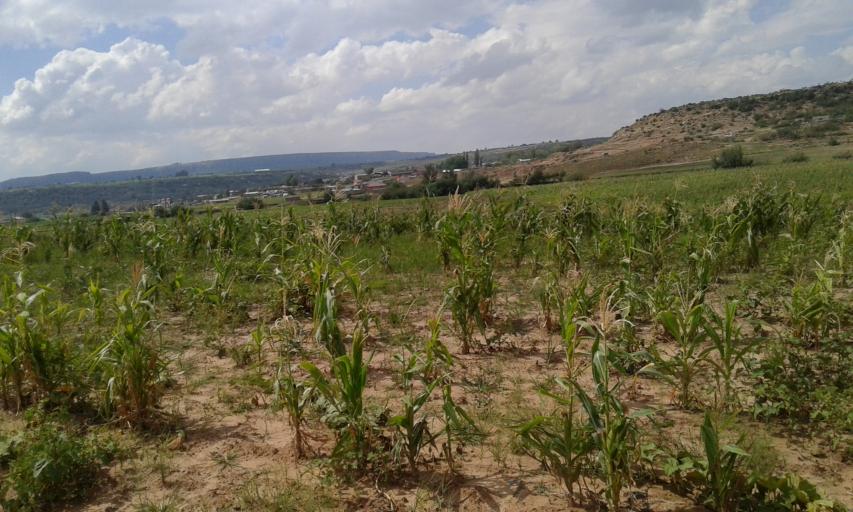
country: LS
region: Maseru
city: Maseru
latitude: -29.4097
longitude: 27.5658
